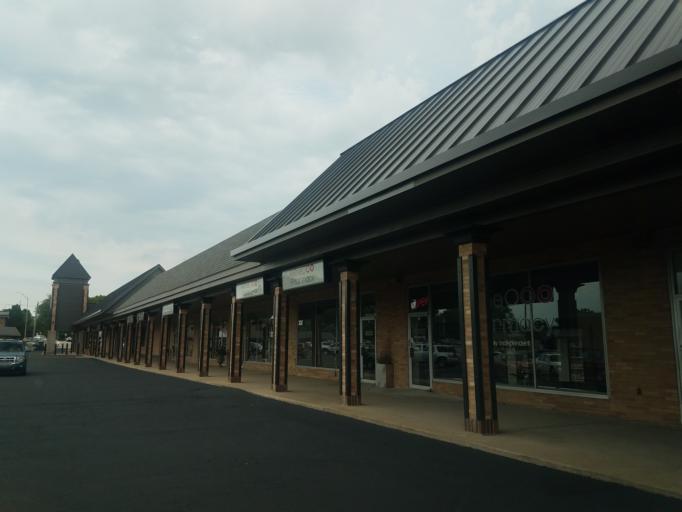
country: US
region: Illinois
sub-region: McLean County
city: Bloomington
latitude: 40.4895
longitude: -88.9707
